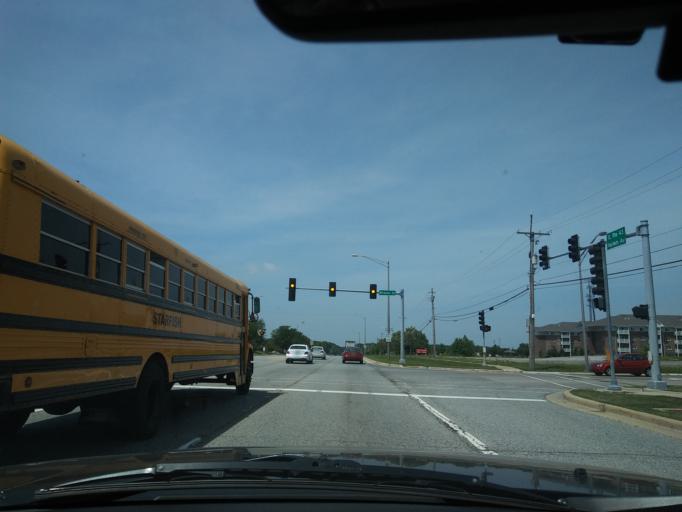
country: US
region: Illinois
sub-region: Cook County
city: Tinley Park
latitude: 41.6088
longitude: -87.7943
